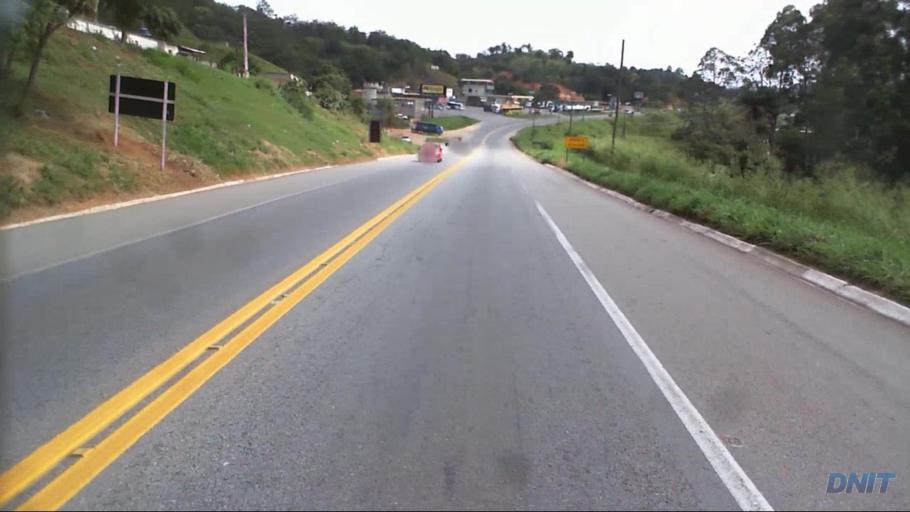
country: BR
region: Minas Gerais
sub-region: Santa Luzia
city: Santa Luzia
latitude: -19.8333
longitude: -43.8472
